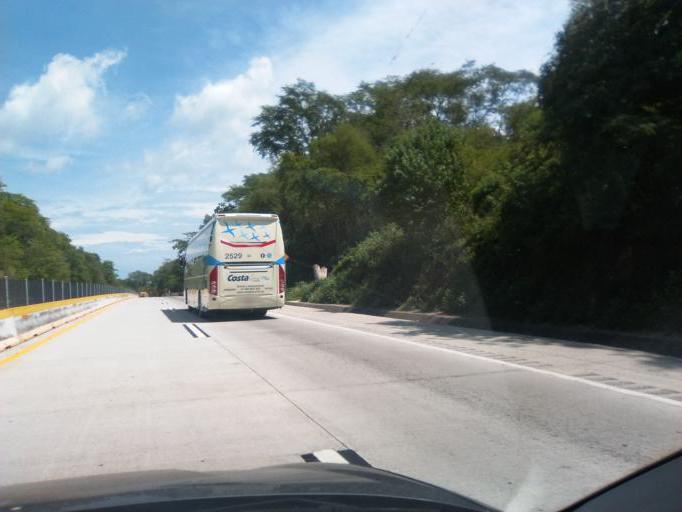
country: MX
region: Guerrero
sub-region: Acapulco de Juarez
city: Colonia Nueva Revolucion
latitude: 16.9311
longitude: -99.7871
